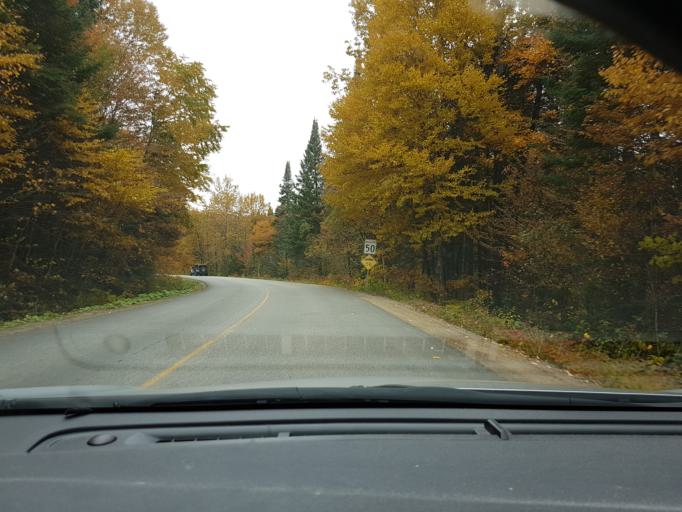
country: CA
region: Quebec
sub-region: Capitale-Nationale
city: Shannon
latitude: 47.1105
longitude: -71.3476
